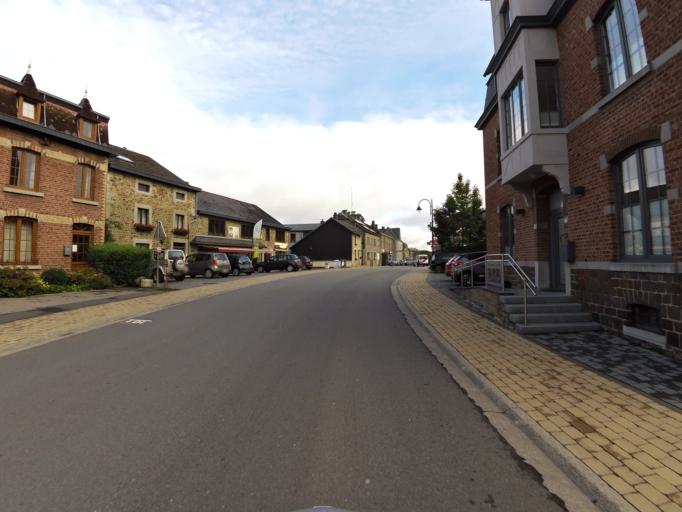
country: BE
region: Wallonia
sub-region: Province du Luxembourg
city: Erezee
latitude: 50.2927
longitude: 5.5581
